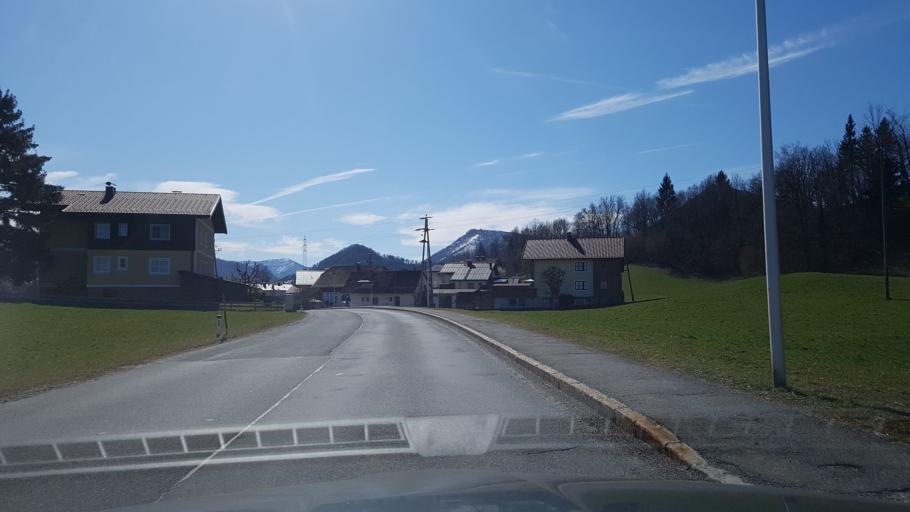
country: AT
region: Salzburg
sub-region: Politischer Bezirk Salzburg-Umgebung
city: Koppl
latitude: 47.8122
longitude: 13.1540
